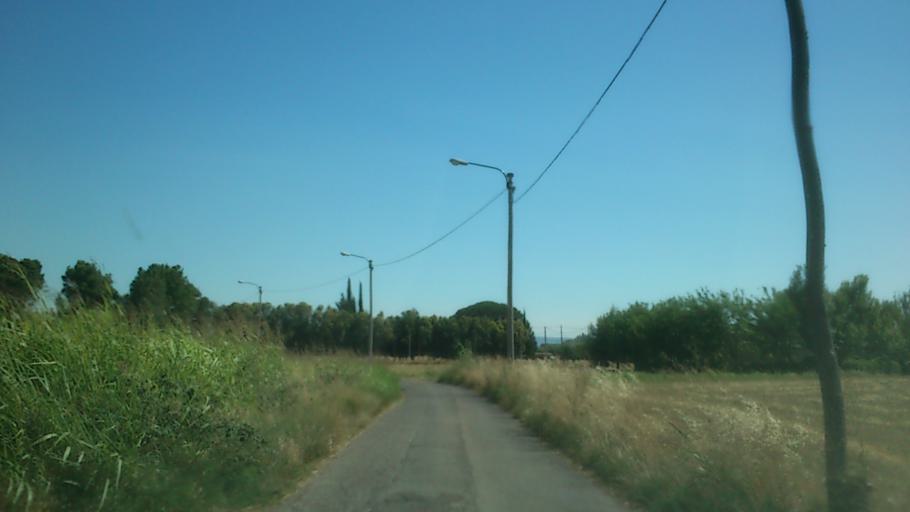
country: ES
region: Aragon
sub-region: Provincia de Zaragoza
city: Villanueva de Gallego
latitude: 41.6944
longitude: -0.8119
